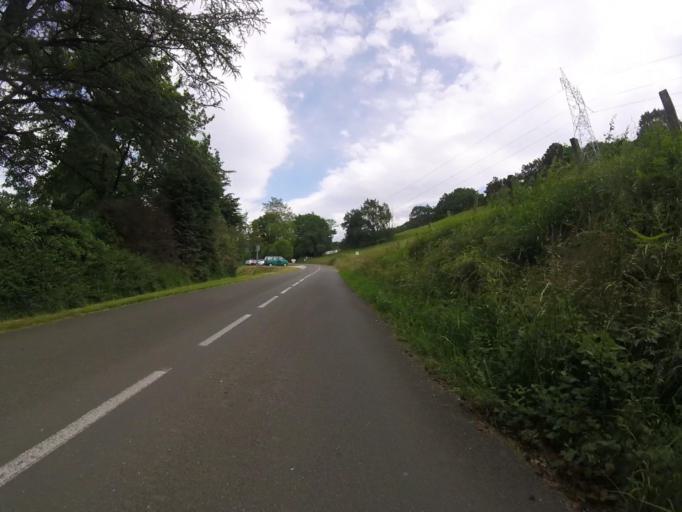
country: ES
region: Basque Country
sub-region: Provincia de Guipuzcoa
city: Errenteria
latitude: 43.2795
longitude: -1.8560
